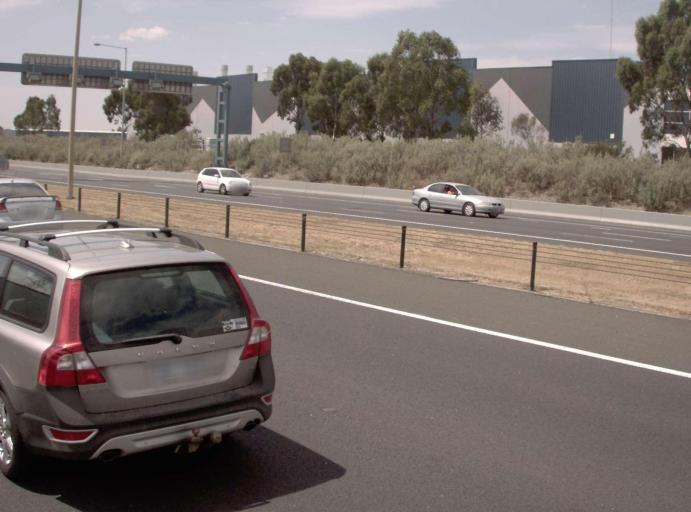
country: AU
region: Victoria
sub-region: Brimbank
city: Sunshine West
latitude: -37.8114
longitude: 144.8078
